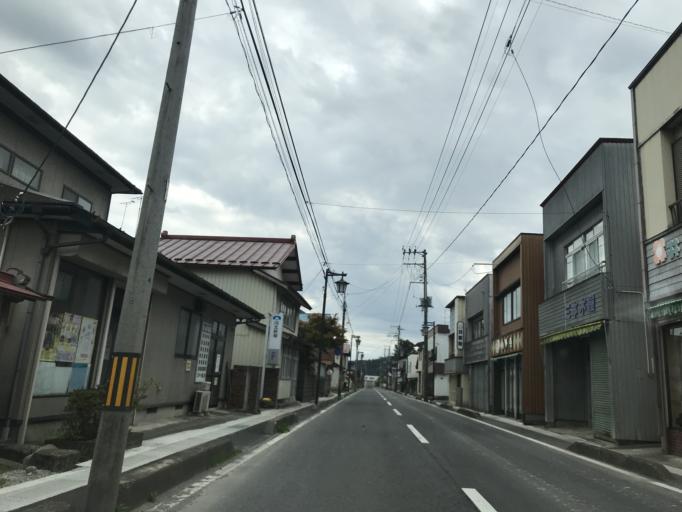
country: JP
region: Iwate
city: Ichinoseki
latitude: 38.7687
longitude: 141.3287
